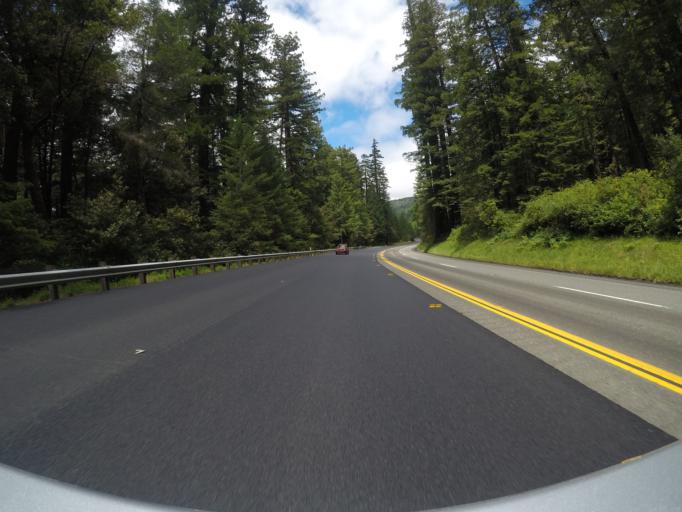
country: US
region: California
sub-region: Humboldt County
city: Redway
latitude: 40.2901
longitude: -123.8963
